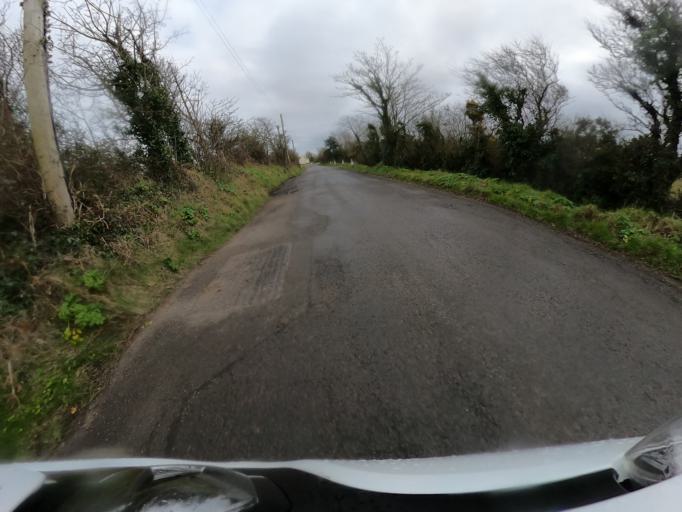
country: IM
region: Ramsey
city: Ramsey
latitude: 54.3768
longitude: -4.4469
